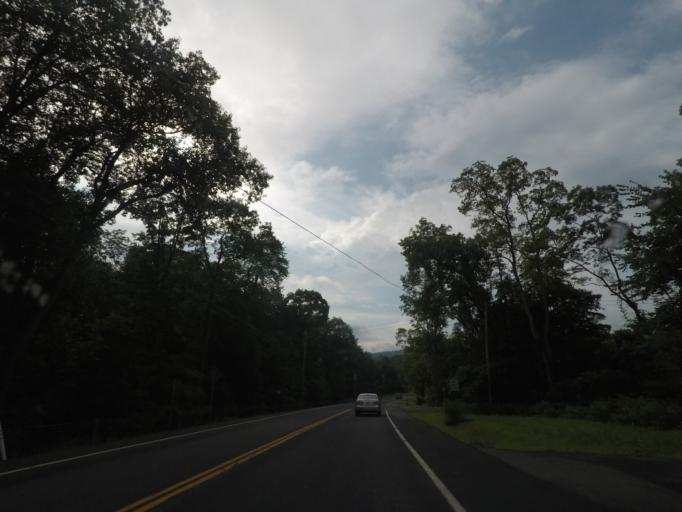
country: US
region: New York
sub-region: Rensselaer County
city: Nassau
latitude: 42.5018
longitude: -73.5584
